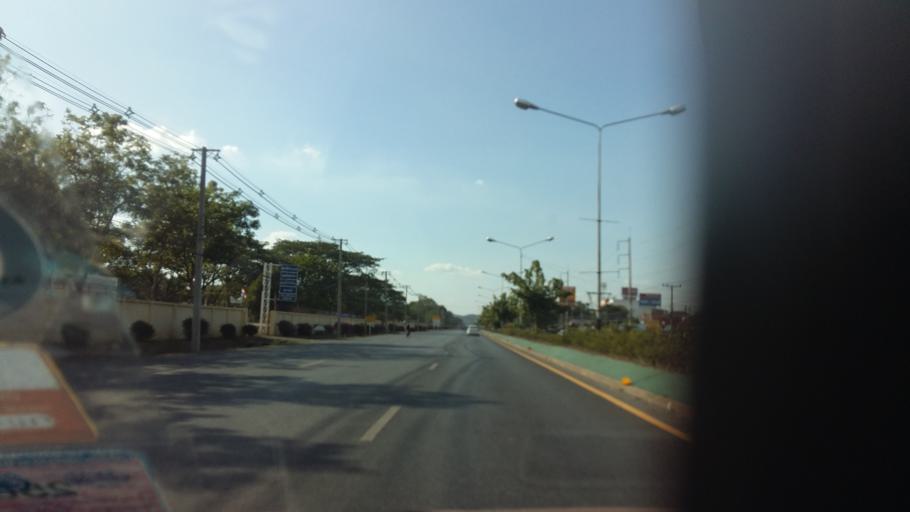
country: TH
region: Lop Buri
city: Lop Buri
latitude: 14.8369
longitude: 100.6448
